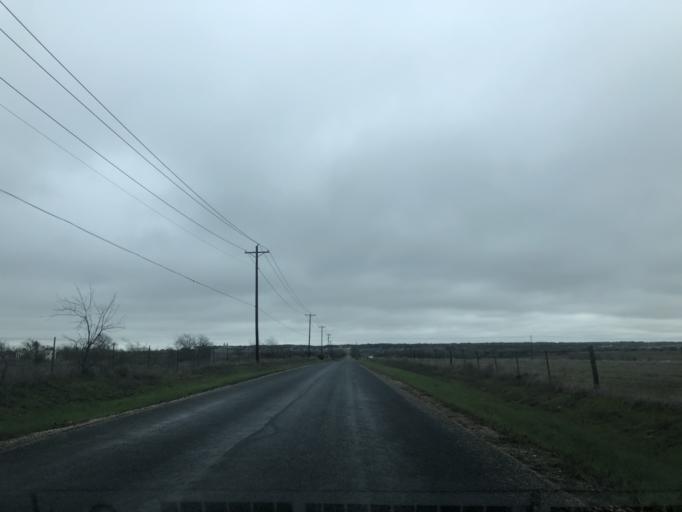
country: US
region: Texas
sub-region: Williamson County
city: Serenada
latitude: 30.7590
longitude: -97.6083
